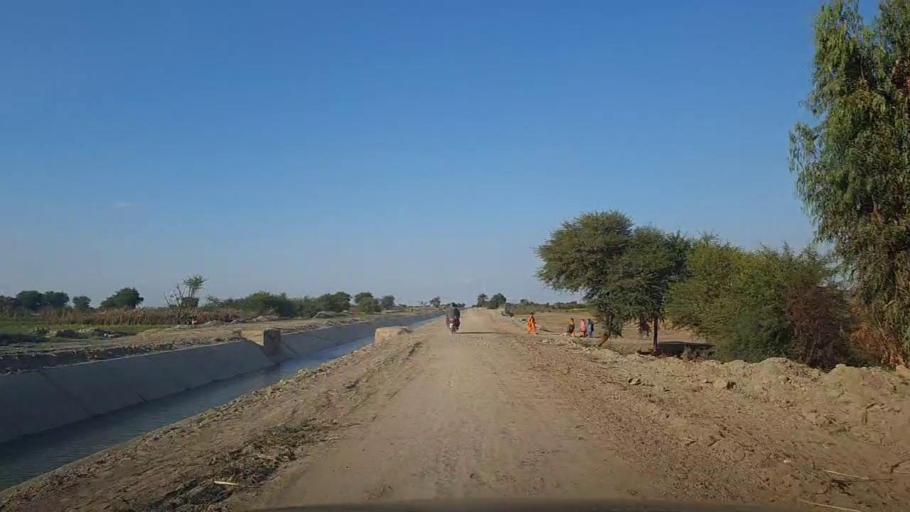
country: PK
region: Sindh
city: Jhol
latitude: 25.9002
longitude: 69.0391
